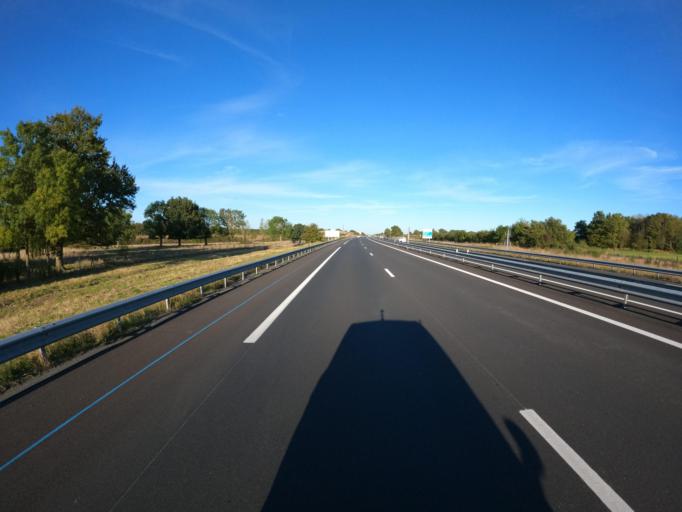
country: FR
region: Pays de la Loire
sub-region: Departement de Maine-et-Loire
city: La Tessoualle
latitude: 47.0097
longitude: -0.8949
